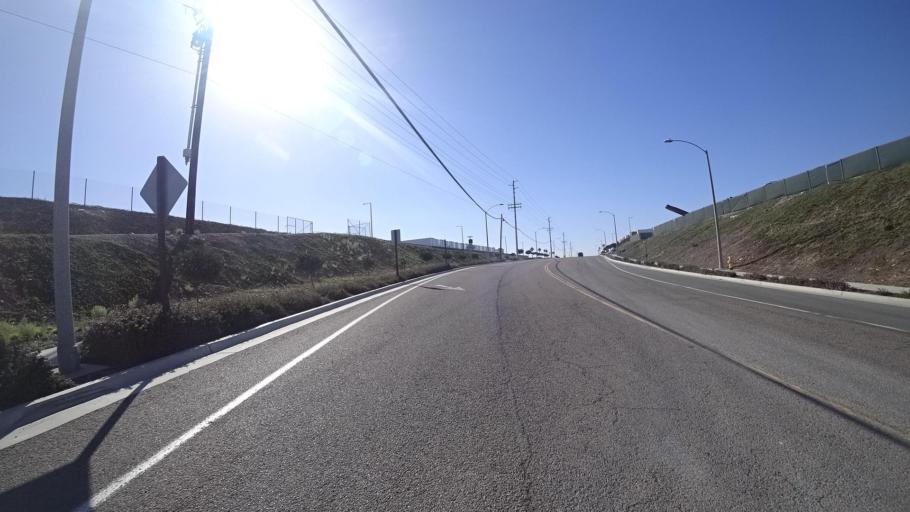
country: MX
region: Baja California
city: Tijuana
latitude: 32.5819
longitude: -116.9191
